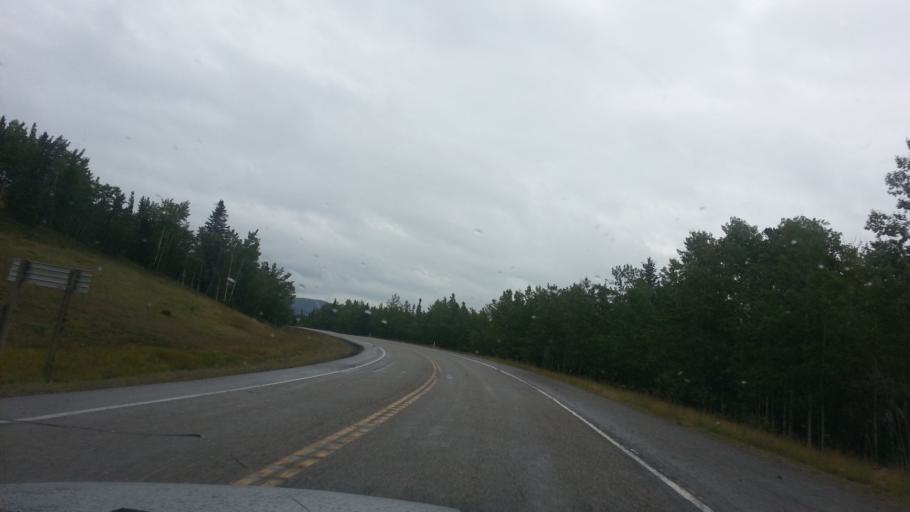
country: CA
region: Alberta
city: Cochrane
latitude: 50.8792
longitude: -114.7148
